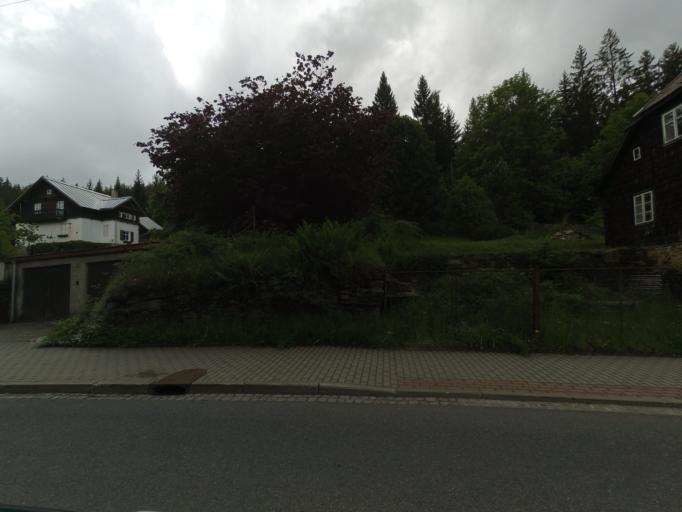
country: CZ
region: Plzensky
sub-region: Okres Klatovy
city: Zelezna Ruda
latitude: 49.2104
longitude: 13.1979
